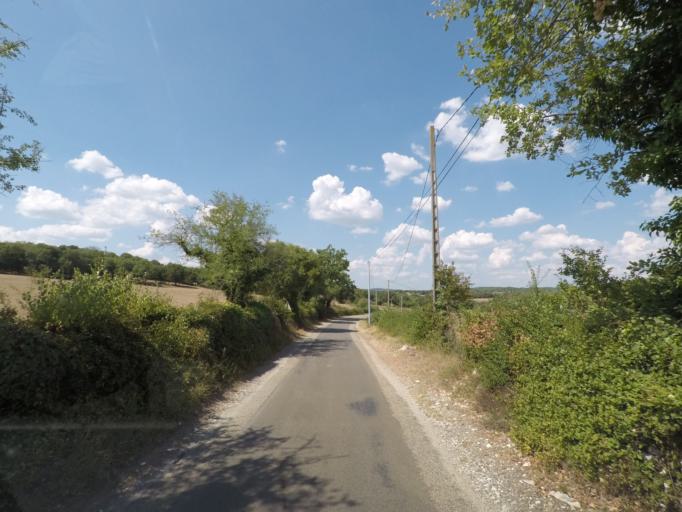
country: FR
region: Midi-Pyrenees
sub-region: Departement du Lot
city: Lalbenque
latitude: 44.5169
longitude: 1.6311
